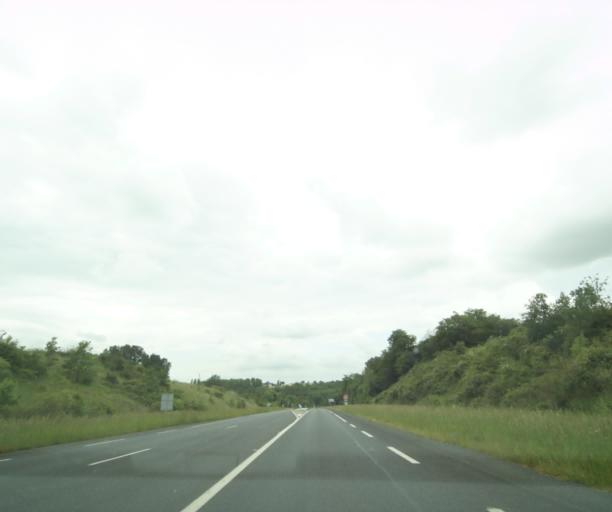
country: FR
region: Poitou-Charentes
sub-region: Departement des Deux-Sevres
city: Saint-Varent
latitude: 46.9116
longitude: -0.1944
